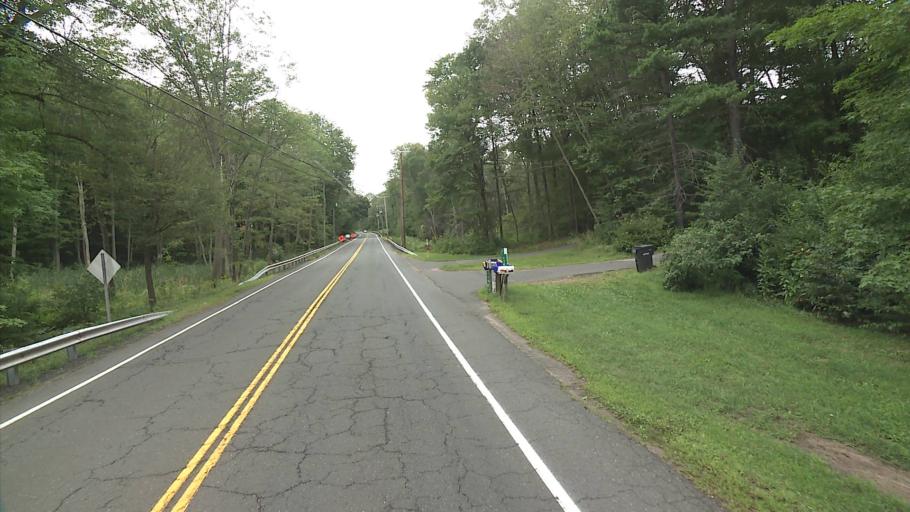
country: US
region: Connecticut
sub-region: Hartford County
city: Manchester
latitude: 41.7625
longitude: -72.4523
